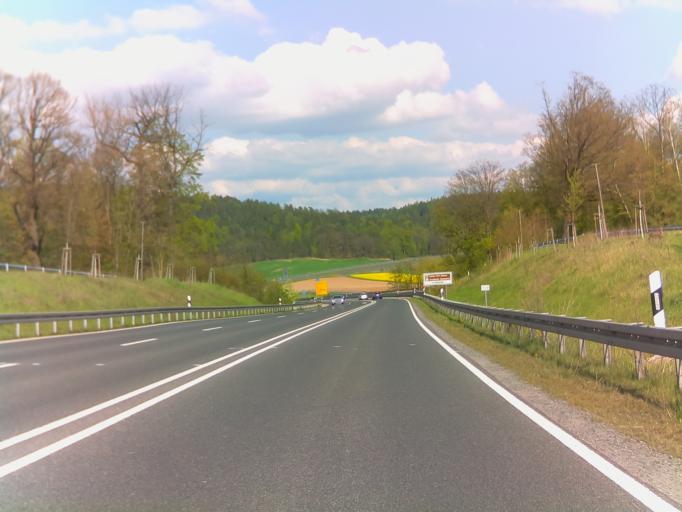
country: DE
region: Bavaria
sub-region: Upper Franconia
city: Rodental
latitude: 50.3064
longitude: 11.0175
